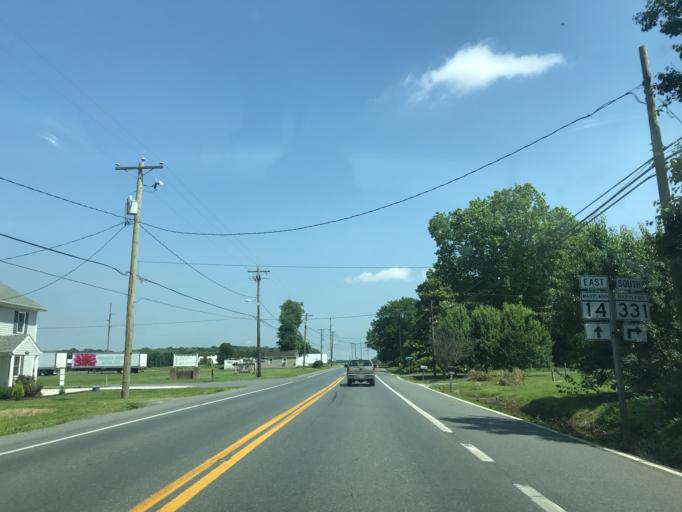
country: US
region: Maryland
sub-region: Dorchester County
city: Hurlock
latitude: 38.5778
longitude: -75.8392
